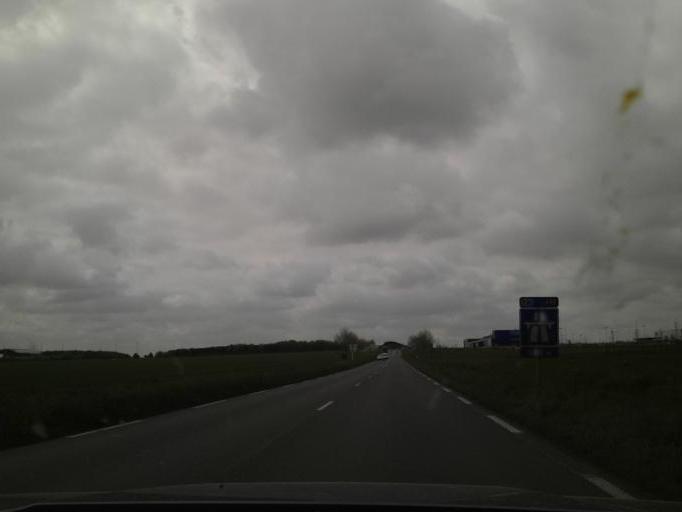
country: FR
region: Pays de la Loire
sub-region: Departement de la Vendee
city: Fontenay-le-Comte
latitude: 46.4414
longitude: -0.8200
